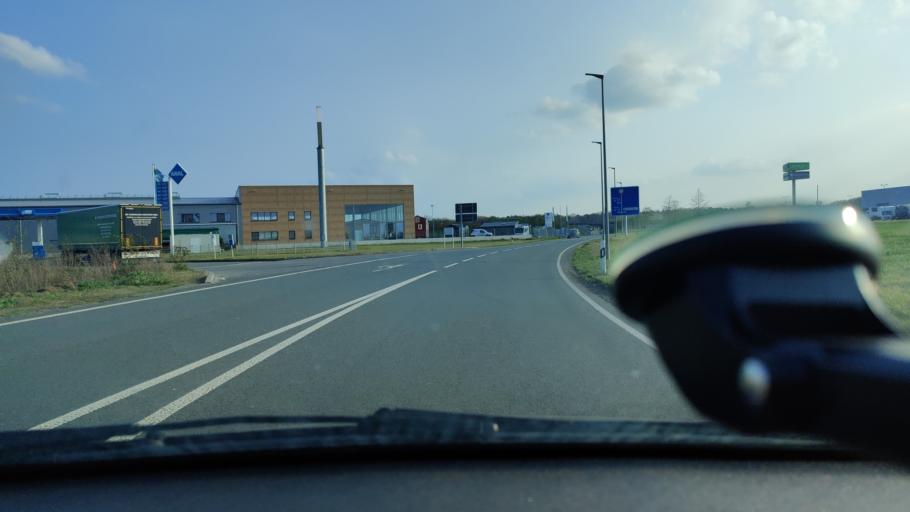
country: DE
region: North Rhine-Westphalia
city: Straelen
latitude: 51.3831
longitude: 6.2443
